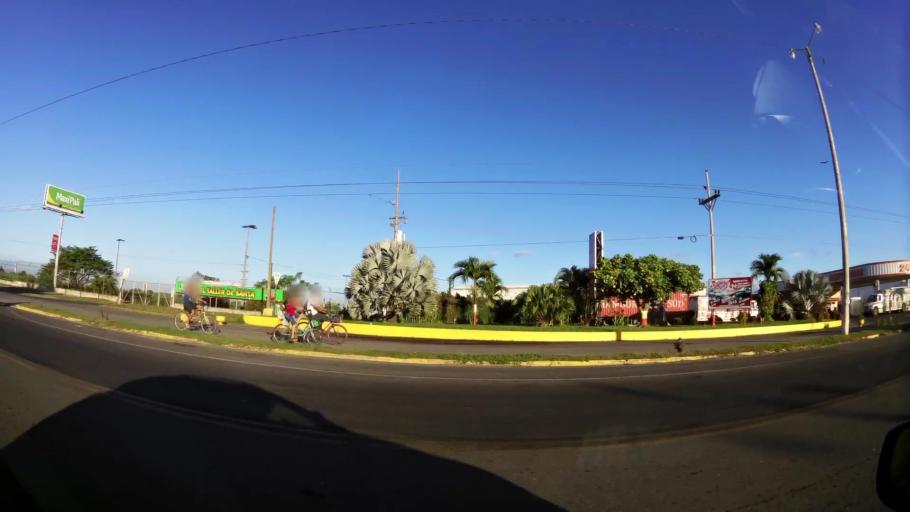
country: CR
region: Puntarenas
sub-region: Canton Central de Puntarenas
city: Chacarita
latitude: 9.9860
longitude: -84.7374
